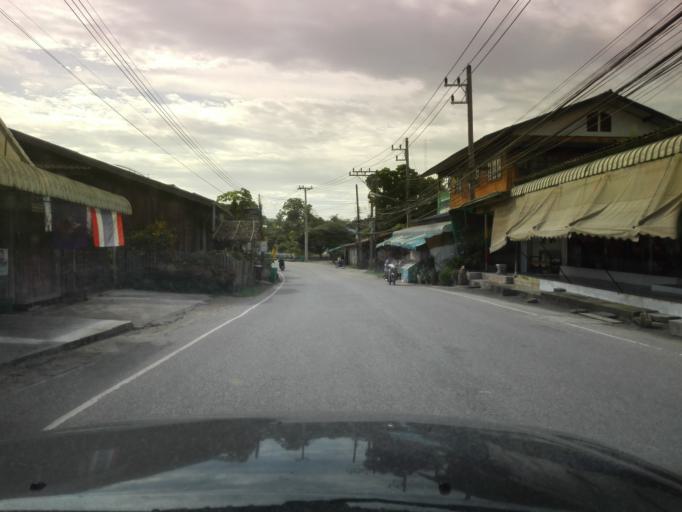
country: TH
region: Tak
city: Mae Ramat
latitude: 16.9811
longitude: 98.5206
